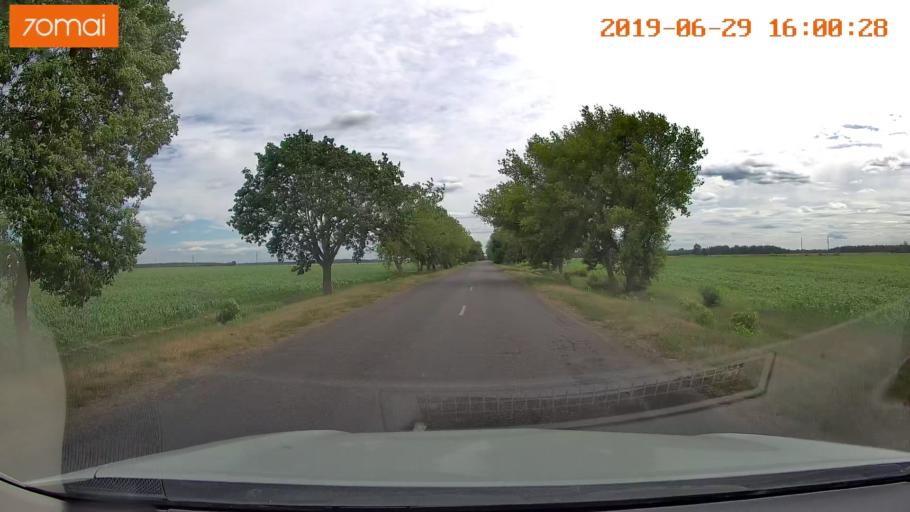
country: BY
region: Brest
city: Luninyets
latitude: 52.2601
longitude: 27.0174
